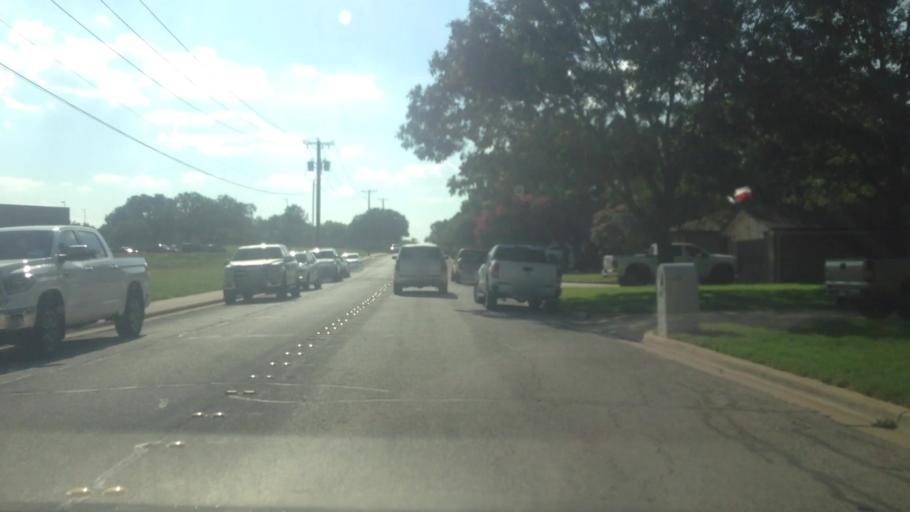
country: US
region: Texas
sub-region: Tarrant County
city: North Richland Hills
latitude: 32.8672
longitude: -97.2005
